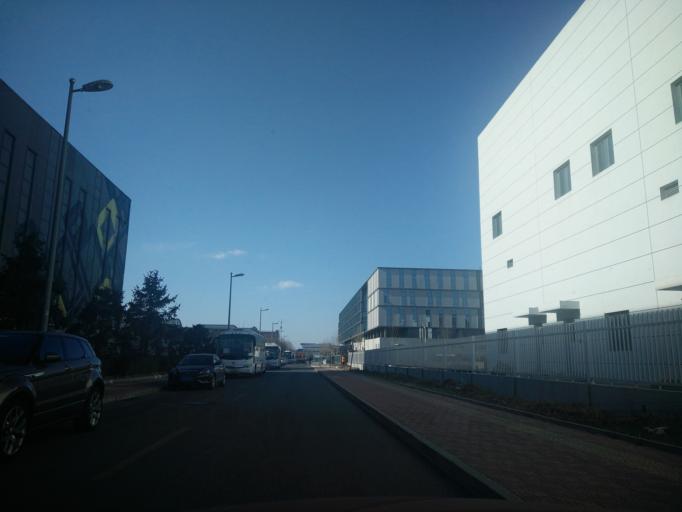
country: CN
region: Beijing
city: Jiugong
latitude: 39.7807
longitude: 116.5254
